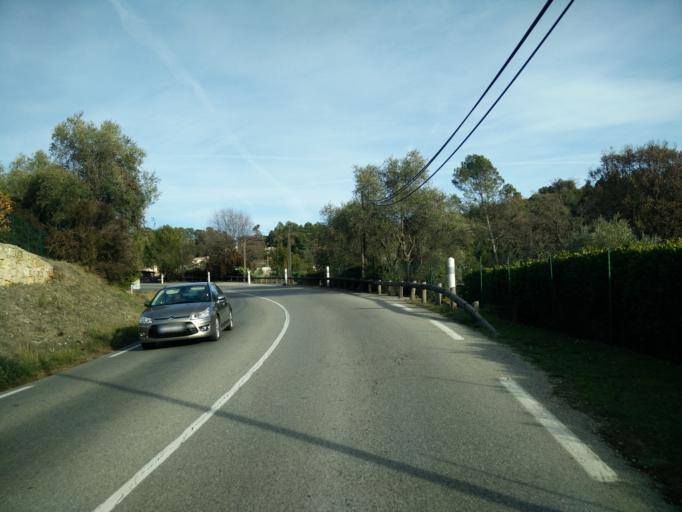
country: FR
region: Provence-Alpes-Cote d'Azur
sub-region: Departement des Alpes-Maritimes
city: Le Tignet
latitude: 43.6291
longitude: 6.8376
